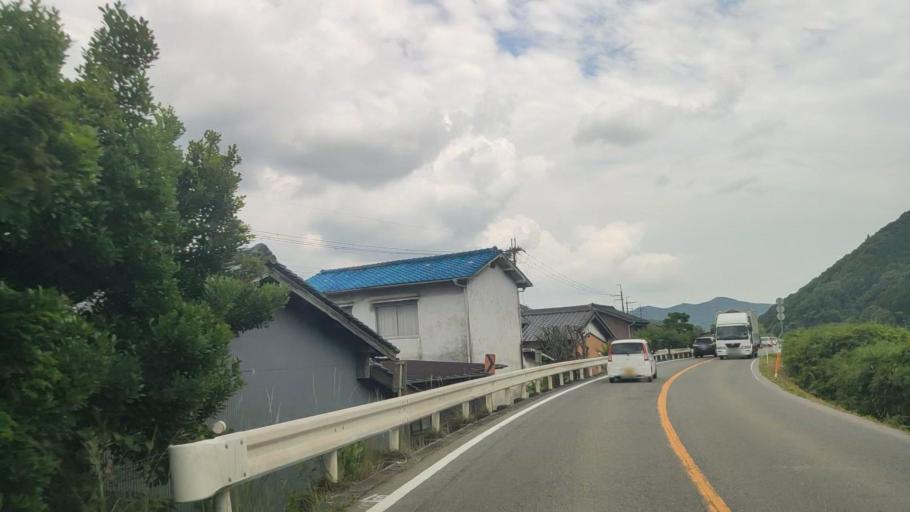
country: JP
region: Hyogo
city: Tatsunocho-tominaga
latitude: 34.9253
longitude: 134.5307
